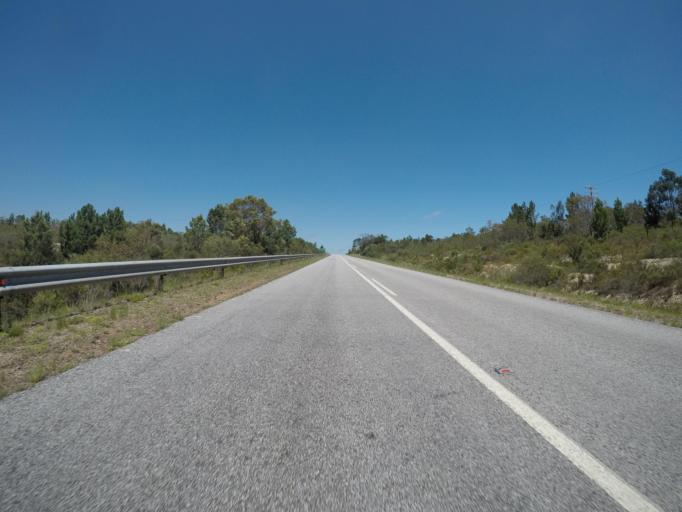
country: ZA
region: Eastern Cape
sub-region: Cacadu District Municipality
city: Kruisfontein
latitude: -34.0256
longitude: 24.5967
